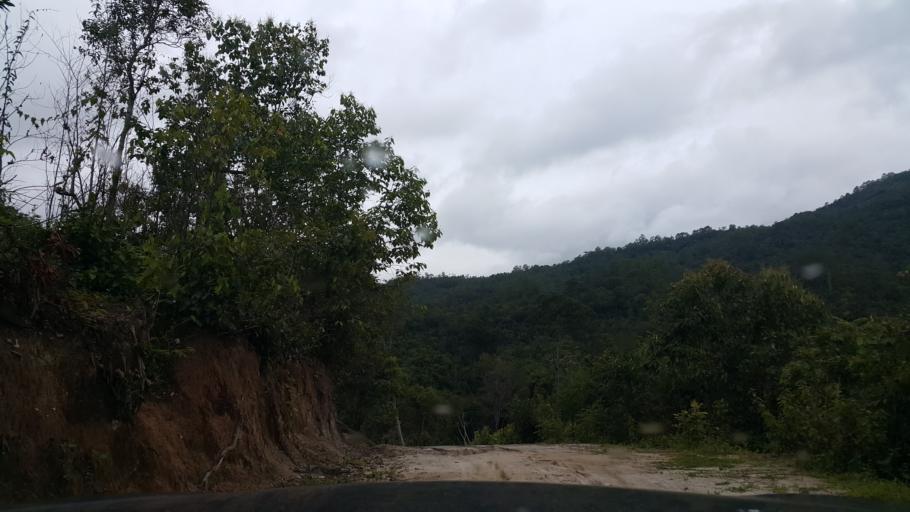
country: TH
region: Chiang Mai
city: Samoeng
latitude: 18.8101
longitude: 98.6248
